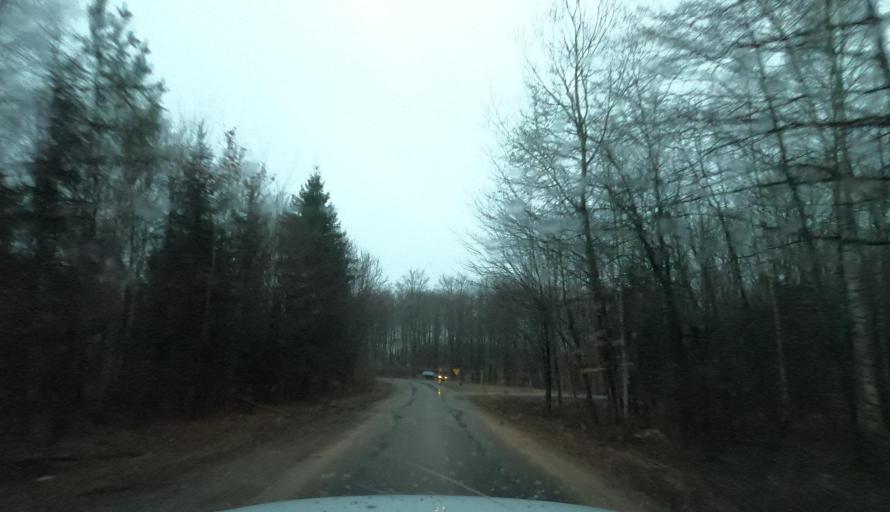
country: PL
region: West Pomeranian Voivodeship
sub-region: Powiat szczecinecki
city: Borne Sulinowo
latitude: 53.6908
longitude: 16.4808
